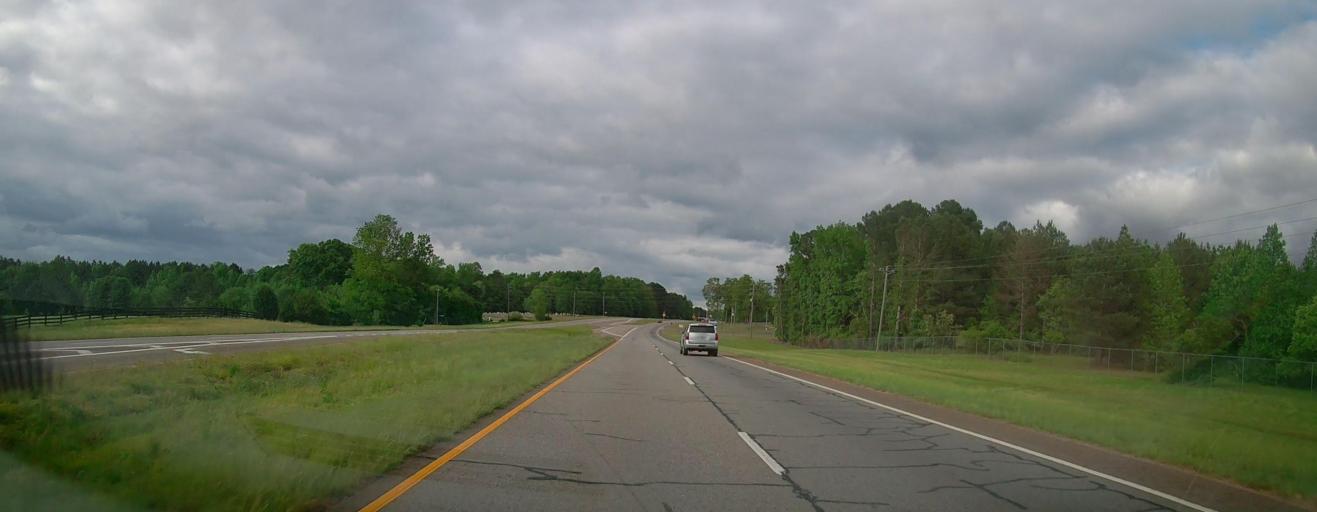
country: US
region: Georgia
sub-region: Oconee County
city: Bogart
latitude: 33.8943
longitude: -83.5795
